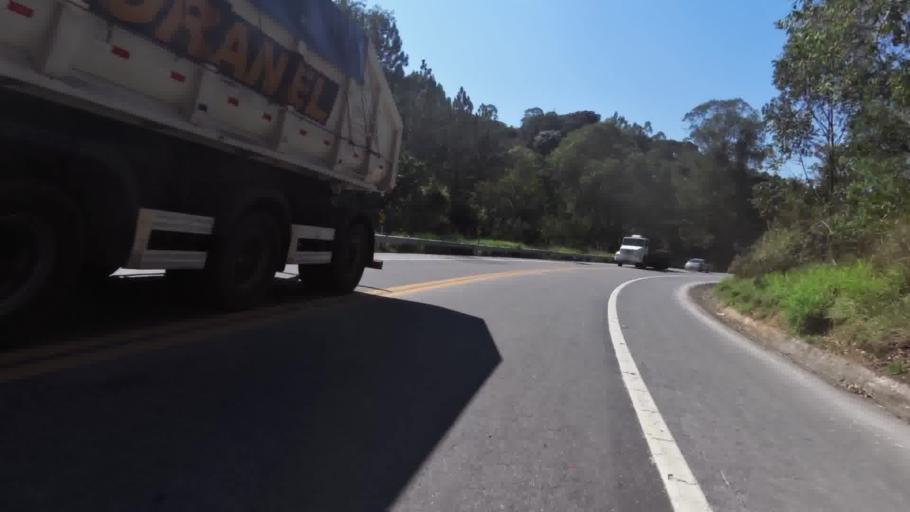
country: BR
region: Espirito Santo
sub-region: Marechal Floriano
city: Marechal Floriano
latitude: -20.4122
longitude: -40.8596
